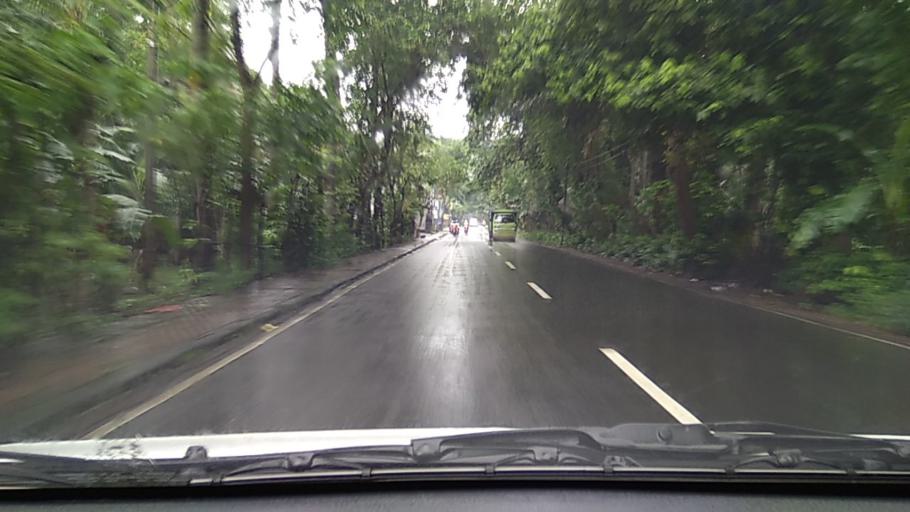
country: ID
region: Bali
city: Banjar Bugbug
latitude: -8.5053
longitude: 115.5787
